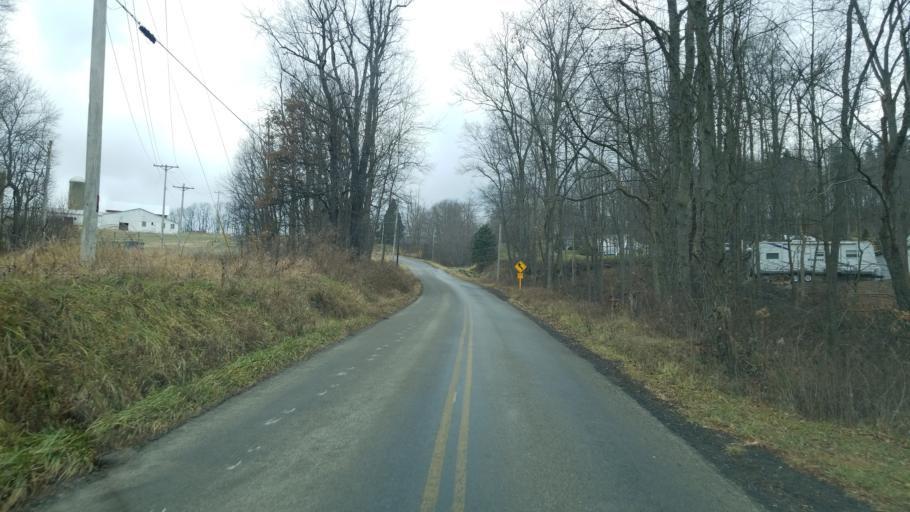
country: US
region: Ohio
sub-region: Holmes County
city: Millersburg
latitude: 40.5691
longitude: -81.9587
